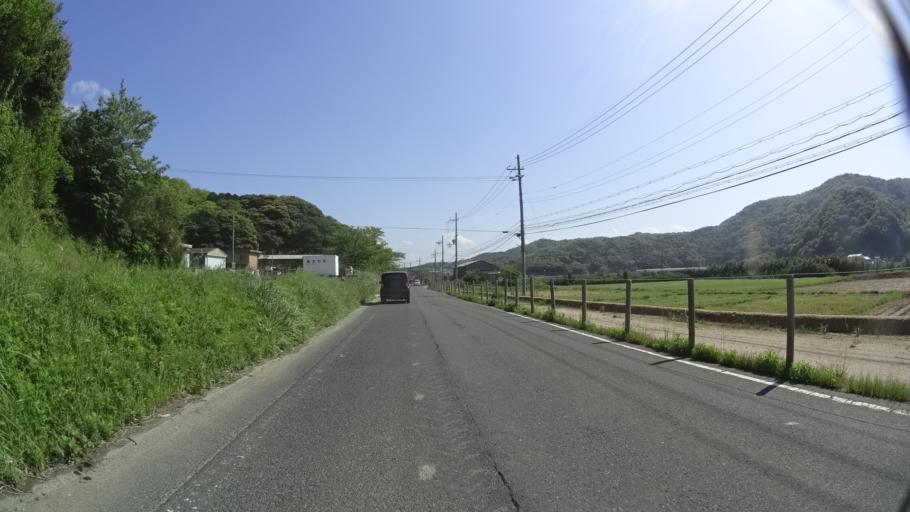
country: JP
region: Kyoto
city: Miyazu
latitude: 35.7302
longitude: 135.1043
